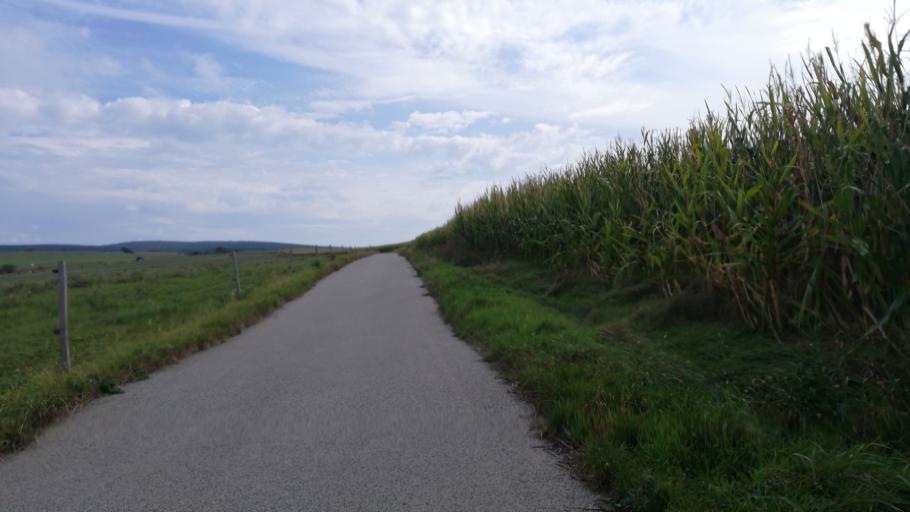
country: CZ
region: South Moravian
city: Sudomerice
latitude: 48.8467
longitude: 17.2723
